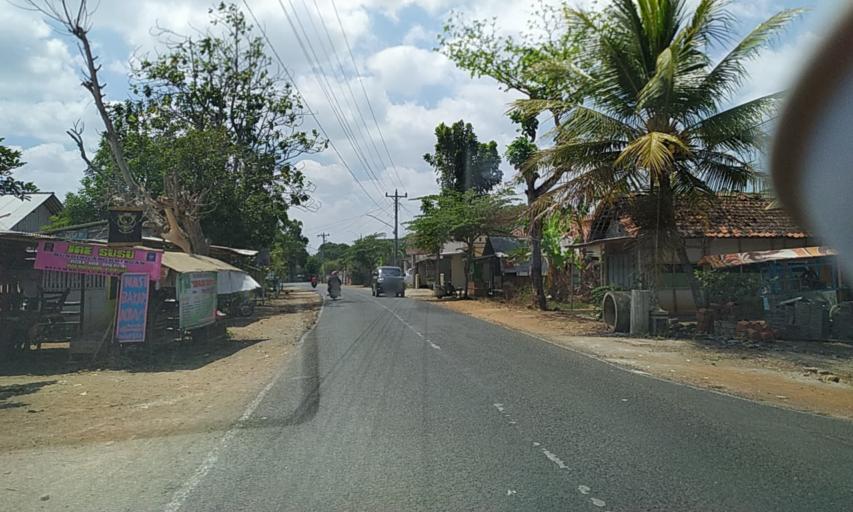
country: ID
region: Central Java
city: Kroya
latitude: -7.6403
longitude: 109.2502
